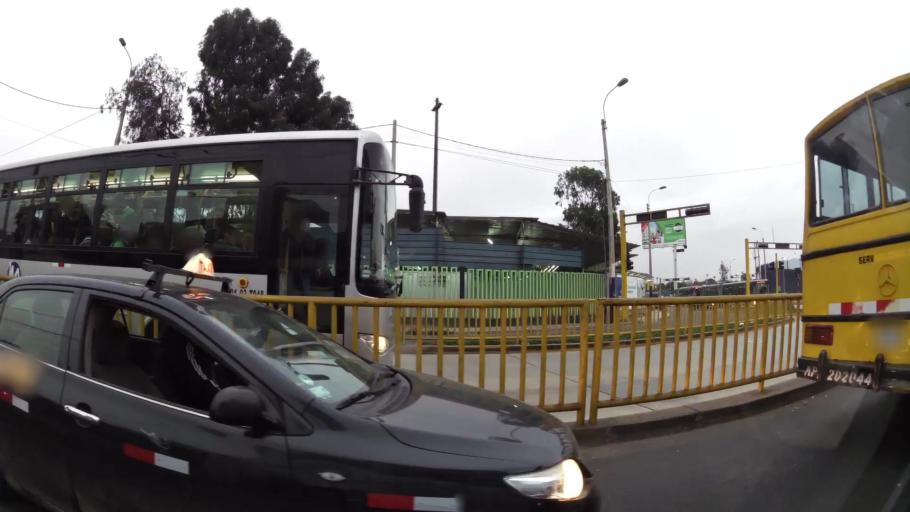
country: PE
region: Lima
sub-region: Lima
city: Surco
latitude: -12.1676
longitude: -77.0197
